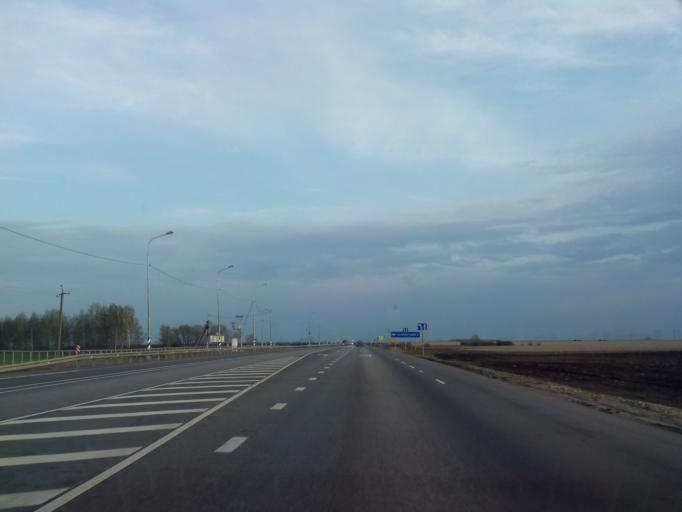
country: RU
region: Rjazan
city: Ryazhsk
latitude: 53.5804
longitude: 40.0424
